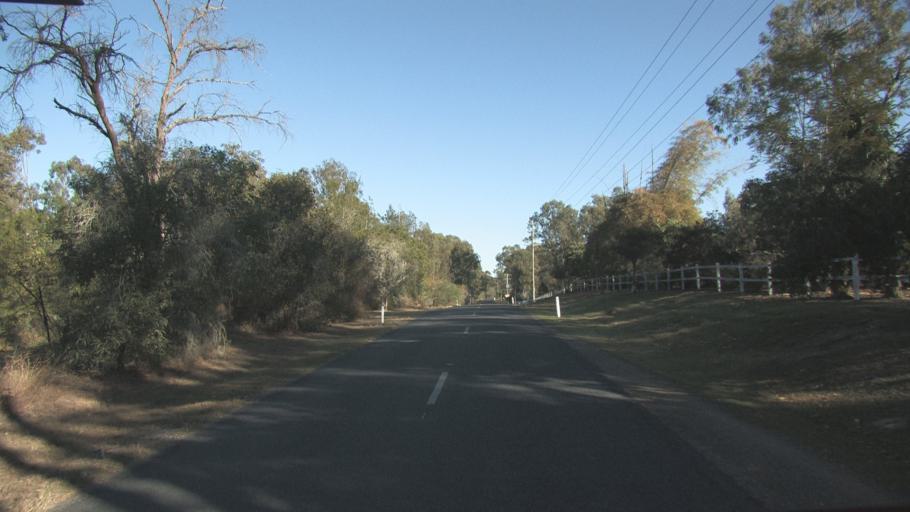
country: AU
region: Queensland
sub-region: Logan
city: North Maclean
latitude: -27.7995
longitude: 152.9997
